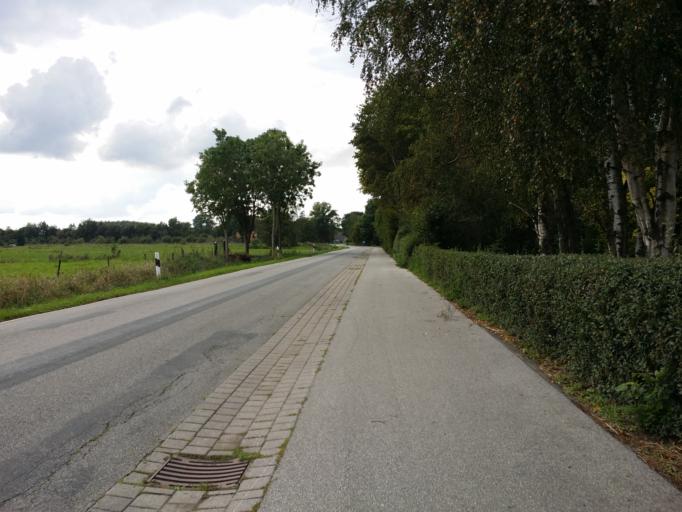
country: DE
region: Lower Saxony
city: Oederquart
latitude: 53.7818
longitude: 9.2518
